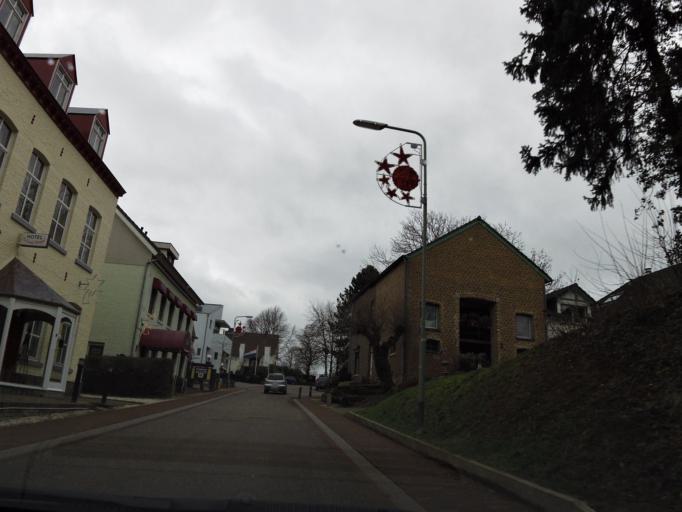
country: BE
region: Flanders
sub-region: Provincie Limburg
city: Sint-Pieters-Voeren
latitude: 50.7668
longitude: 5.8629
